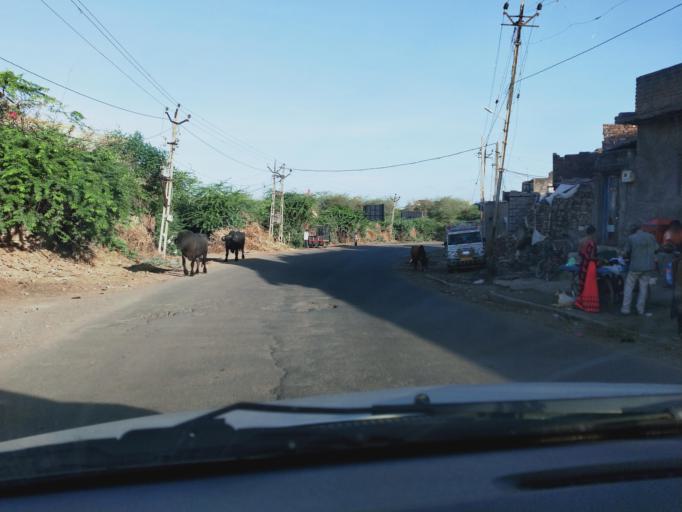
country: IN
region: Gujarat
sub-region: Bhavnagar
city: Bhavnagar
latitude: 21.7282
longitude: 72.1573
